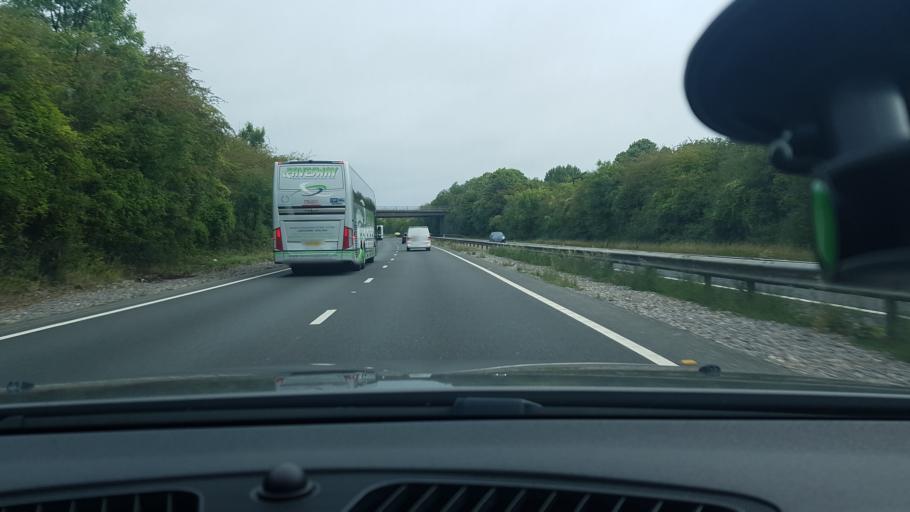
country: GB
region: England
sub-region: Hampshire
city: Overton
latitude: 51.2460
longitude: -1.3405
